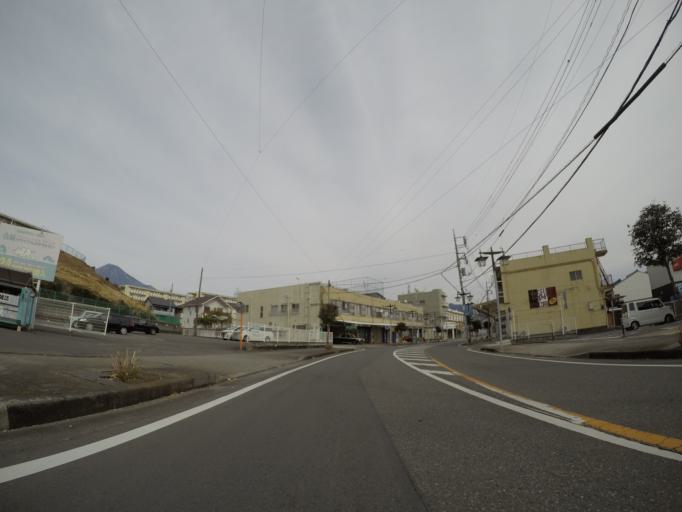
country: JP
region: Shizuoka
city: Fuji
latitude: 35.1863
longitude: 138.6859
